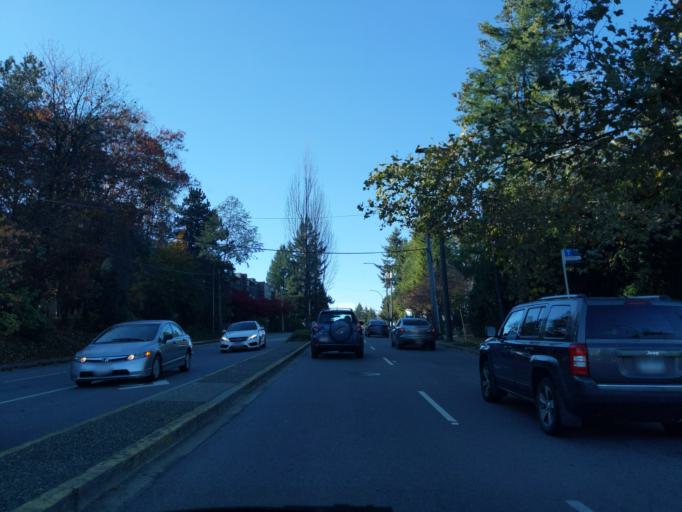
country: CA
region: British Columbia
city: New Westminster
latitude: 49.1862
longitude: -122.8521
